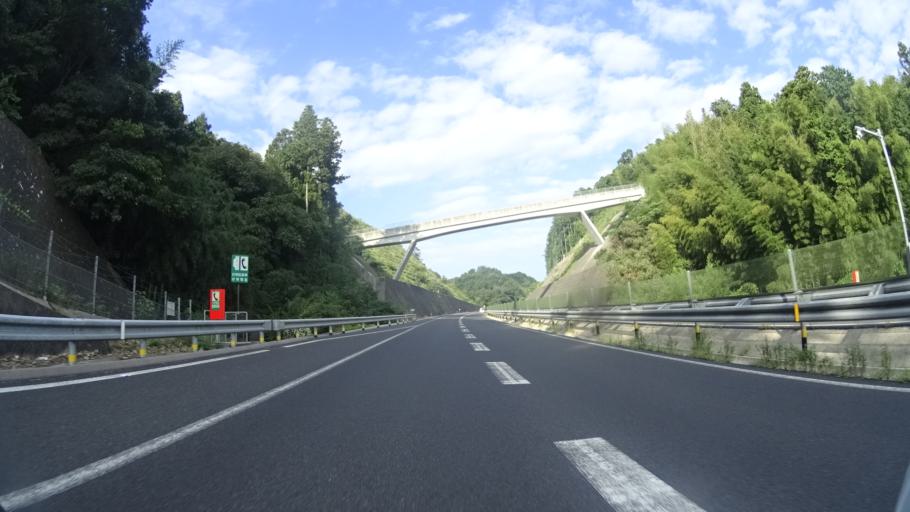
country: JP
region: Shimane
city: Izumo
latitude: 35.3384
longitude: 132.8091
